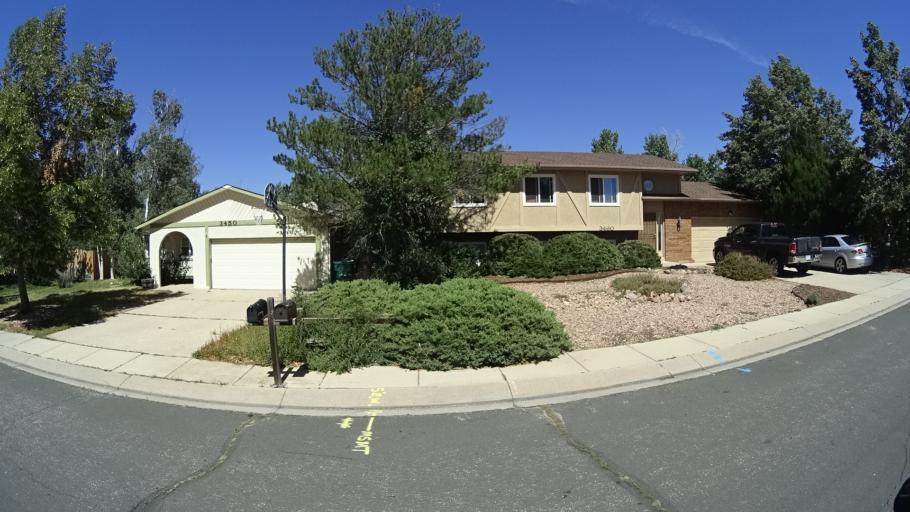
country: US
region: Colorado
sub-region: El Paso County
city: Black Forest
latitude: 38.9433
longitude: -104.7605
